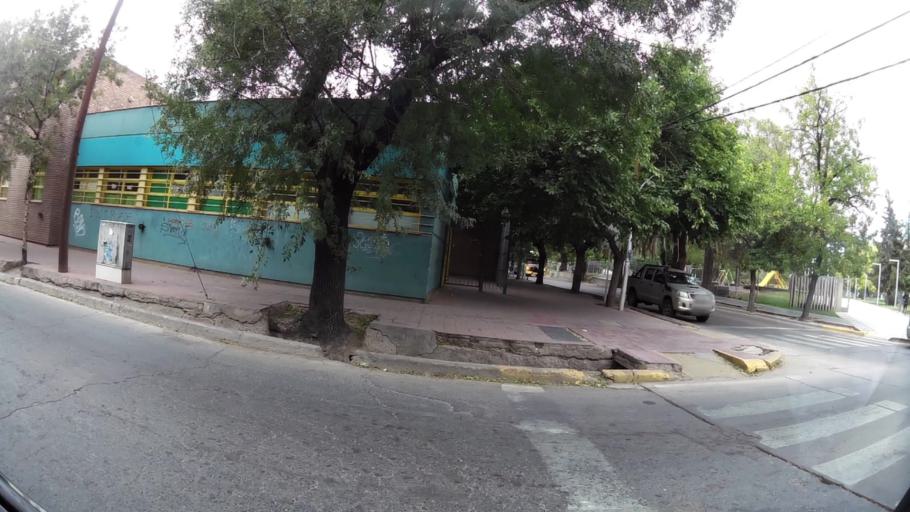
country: AR
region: Mendoza
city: Mendoza
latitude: -32.8877
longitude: -68.8313
